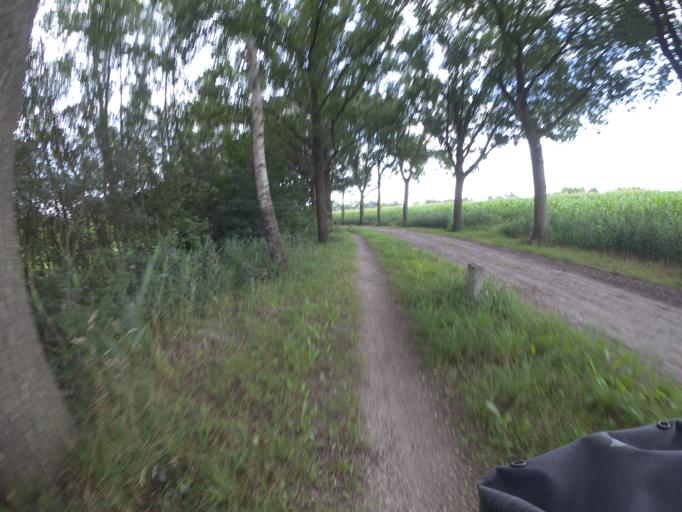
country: NL
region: North Brabant
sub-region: Gemeente Boxtel
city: Boxtel
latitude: 51.5712
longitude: 5.3079
